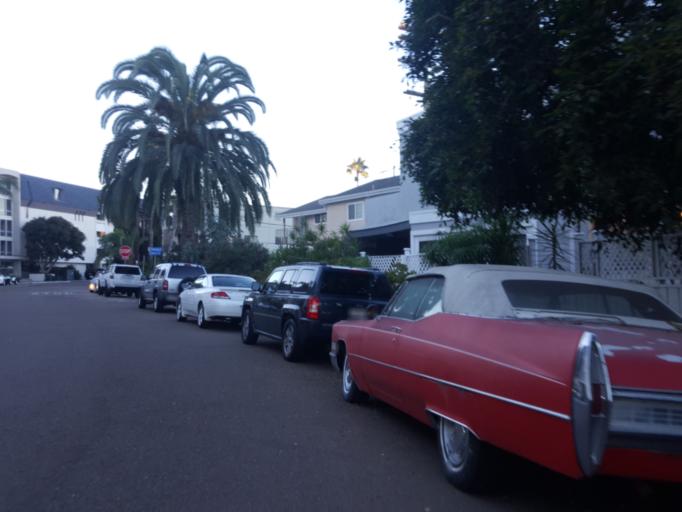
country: US
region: California
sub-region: San Diego County
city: La Jolla
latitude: 32.7946
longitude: -117.2307
